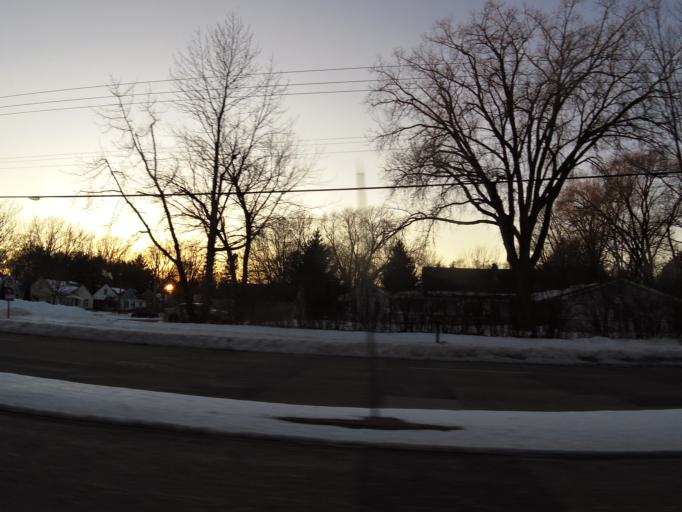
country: US
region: Minnesota
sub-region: Ramsey County
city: White Bear Lake
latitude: 45.0650
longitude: -93.0154
